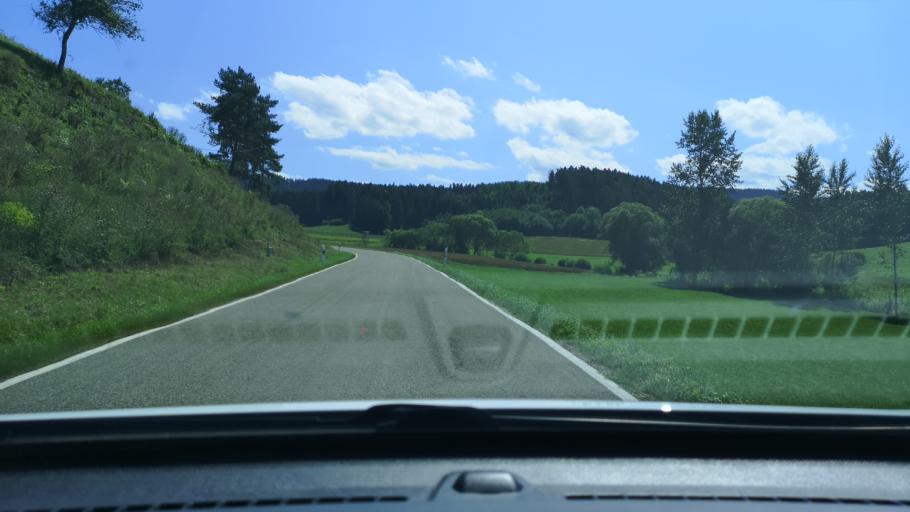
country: DE
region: Baden-Wuerttemberg
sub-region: Freiburg Region
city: Muhlheim am Bach
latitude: 48.3643
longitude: 8.7094
